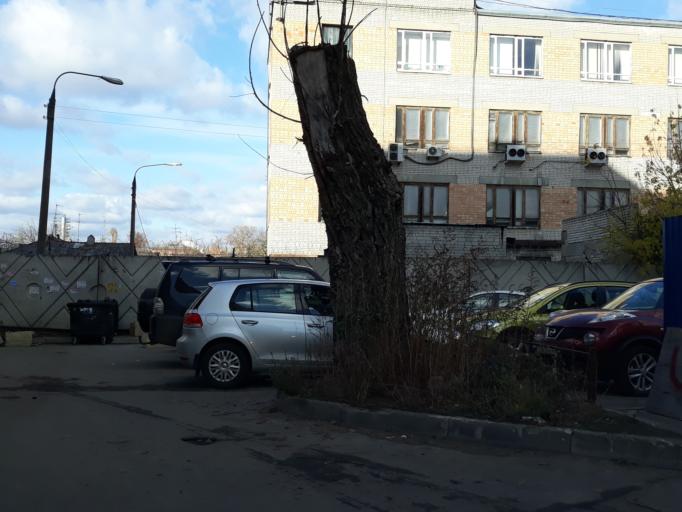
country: RU
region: Nizjnij Novgorod
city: Nizhniy Novgorod
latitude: 56.3040
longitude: 43.9360
